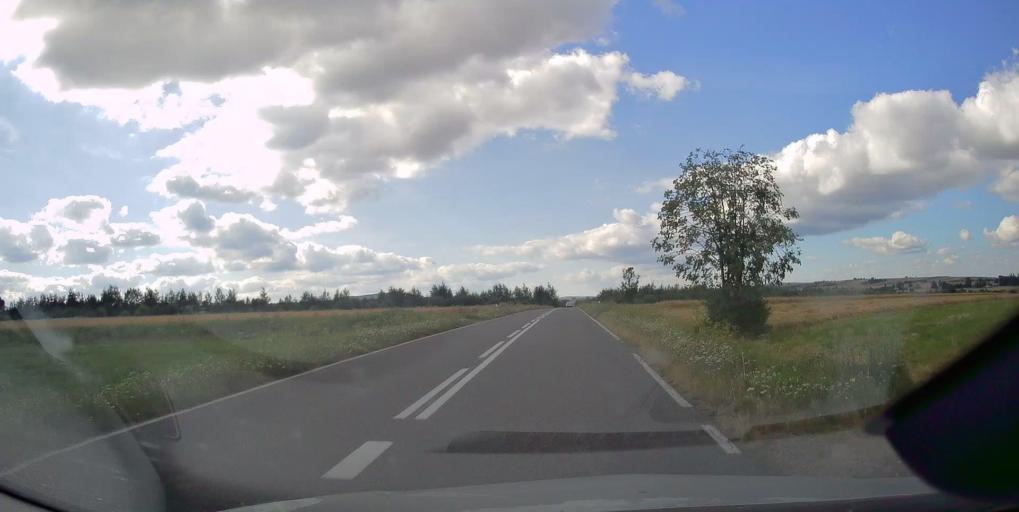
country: PL
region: Swietokrzyskie
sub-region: Powiat kielecki
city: Bodzentyn
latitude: 50.9038
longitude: 21.0129
